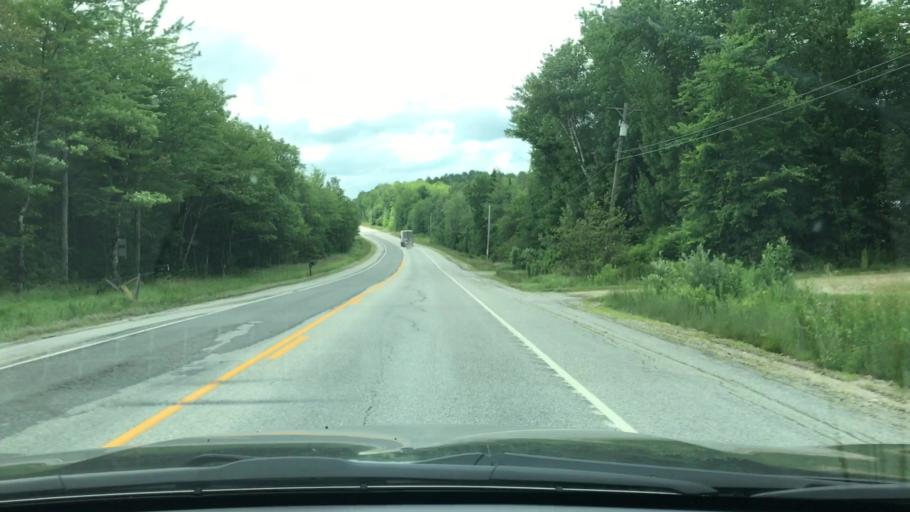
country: US
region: Maine
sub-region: Oxford County
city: West Paris
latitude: 44.3653
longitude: -70.5907
